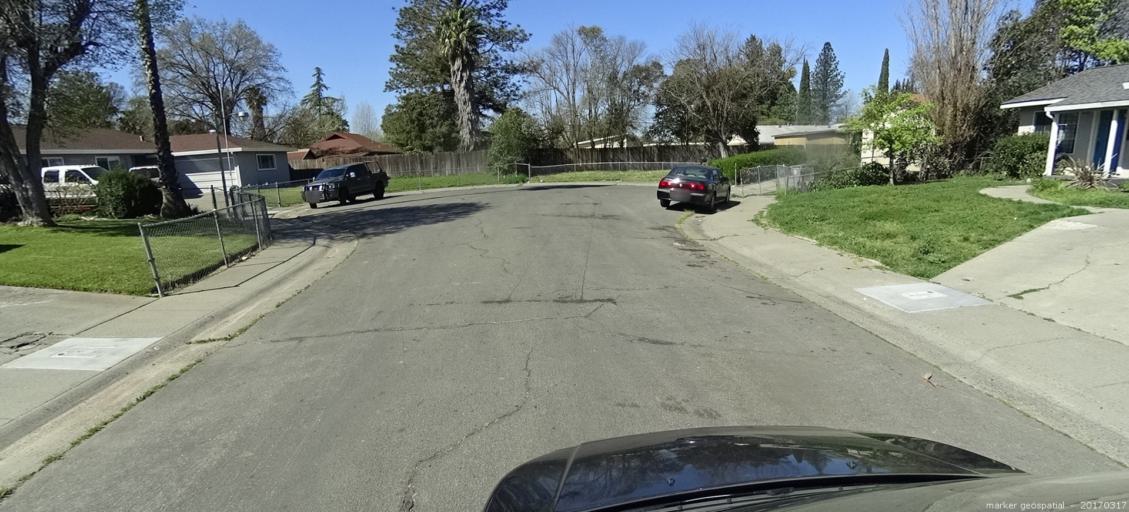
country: US
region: California
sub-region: Sacramento County
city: Parkway
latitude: 38.4838
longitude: -121.4956
